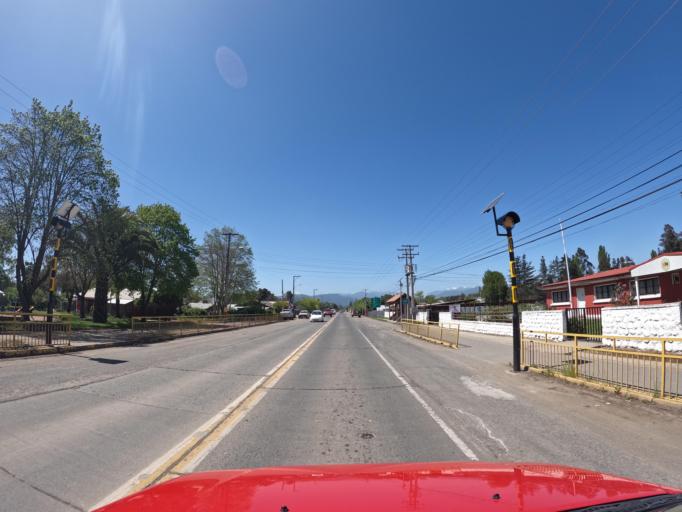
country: CL
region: Maule
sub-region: Provincia de Linares
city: Linares
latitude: -35.8305
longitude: -71.5143
